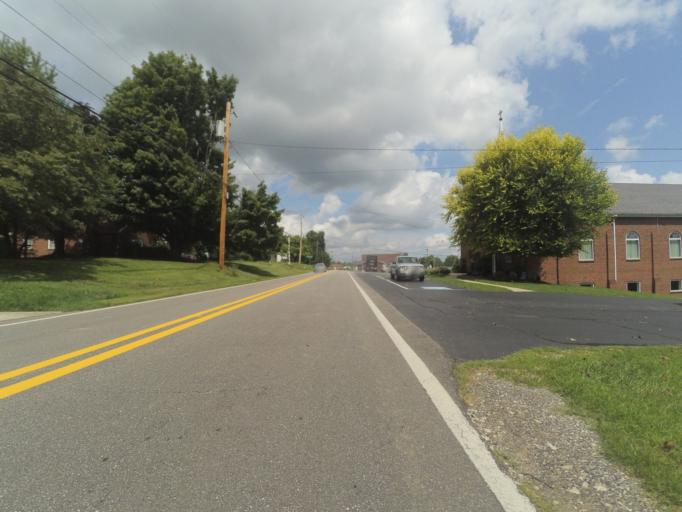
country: US
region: West Virginia
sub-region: Cabell County
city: Pea Ridge
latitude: 38.4096
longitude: -82.3413
